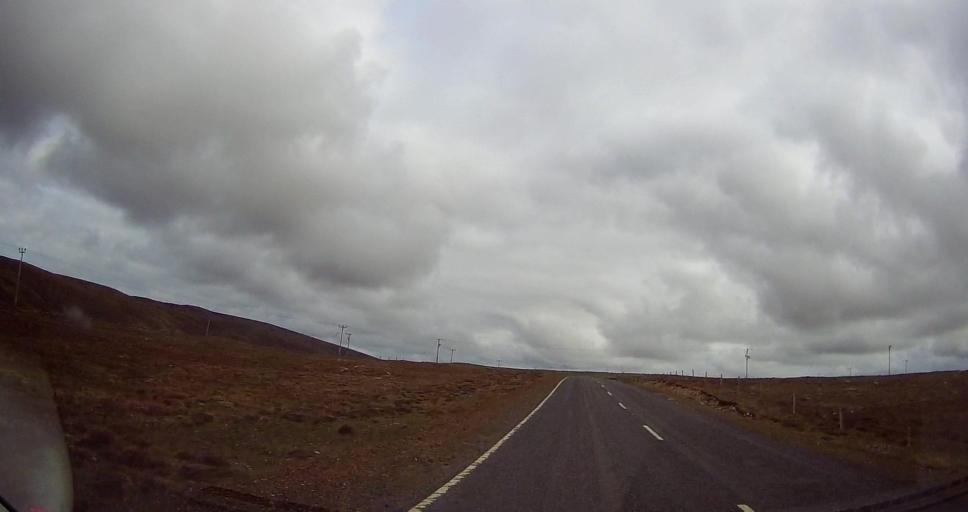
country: GB
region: Scotland
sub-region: Shetland Islands
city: Shetland
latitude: 60.7181
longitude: -0.9124
